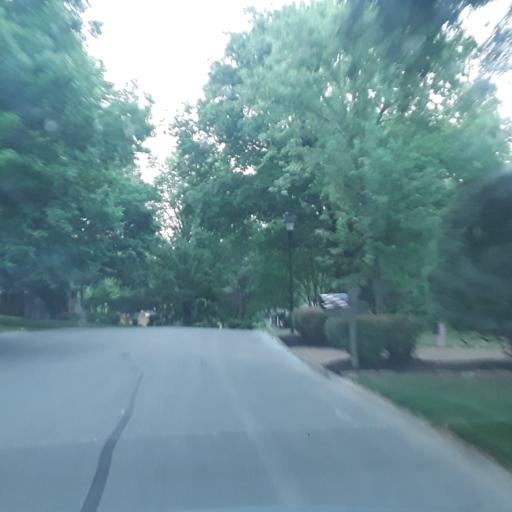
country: US
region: Tennessee
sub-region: Williamson County
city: Brentwood
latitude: 36.0469
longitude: -86.7602
